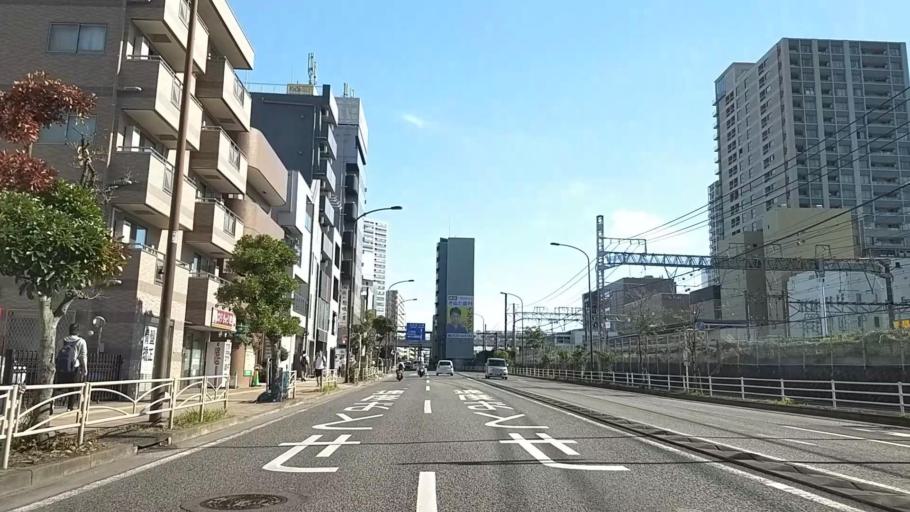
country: JP
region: Kanagawa
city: Yokohama
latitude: 35.4766
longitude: 139.6314
